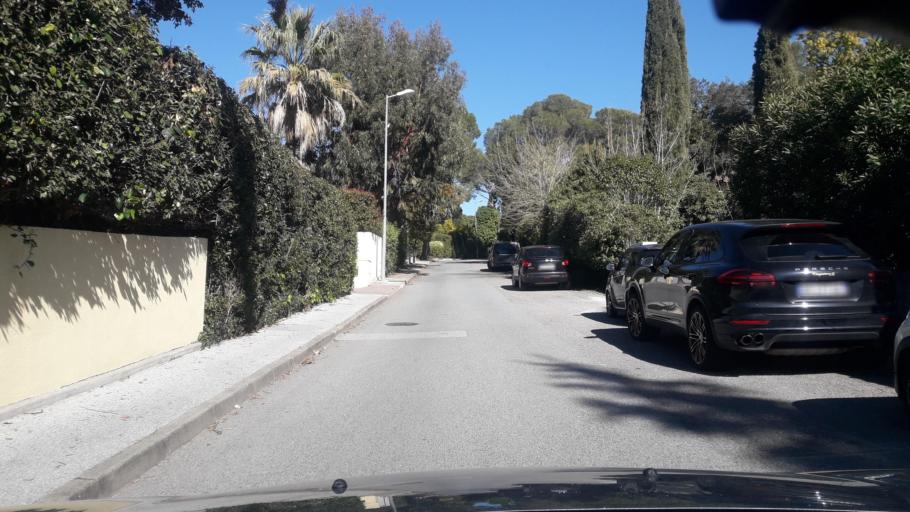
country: FR
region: Provence-Alpes-Cote d'Azur
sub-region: Departement du Var
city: Saint-Raphael
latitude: 43.4478
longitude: 6.7757
